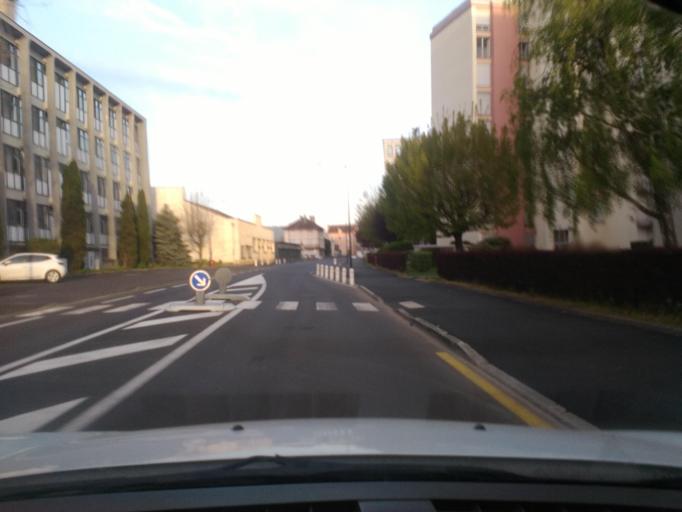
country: FR
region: Franche-Comte
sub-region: Departement de la Haute-Saone
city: Navenne
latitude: 47.6171
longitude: 6.1581
